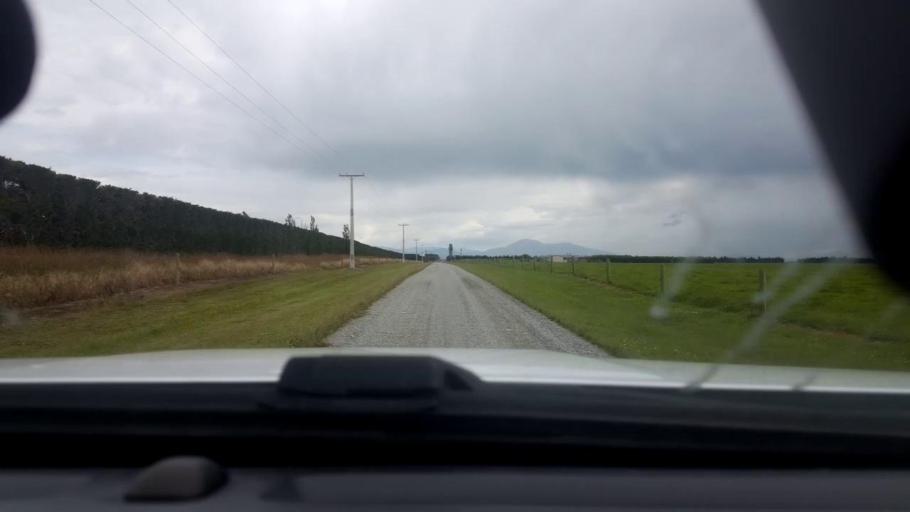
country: NZ
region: Canterbury
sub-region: Timaru District
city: Timaru
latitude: -44.1755
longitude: 171.4197
